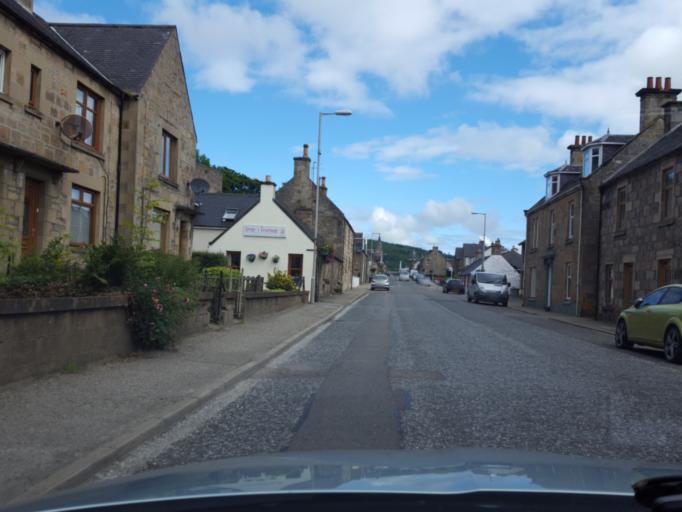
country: GB
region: Scotland
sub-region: Moray
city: Rothes
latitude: 57.5234
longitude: -3.2087
